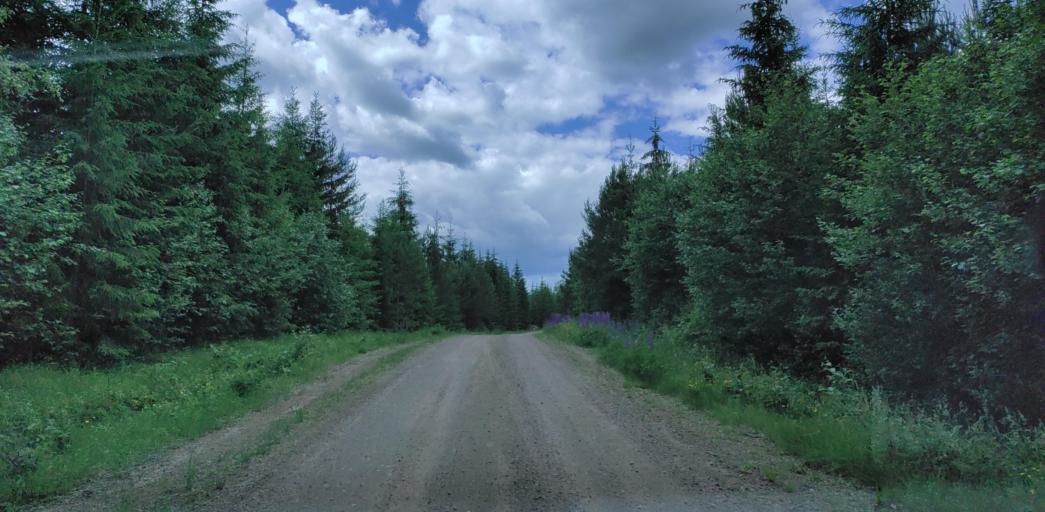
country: SE
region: Vaermland
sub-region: Hagfors Kommun
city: Ekshaerad
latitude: 60.0879
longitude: 13.4331
